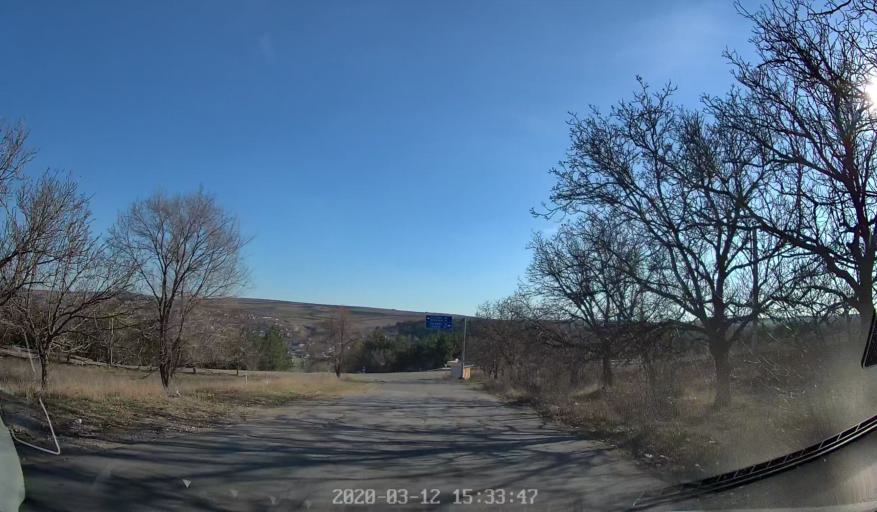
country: MD
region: Chisinau
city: Ciorescu
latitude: 47.1400
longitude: 28.9377
